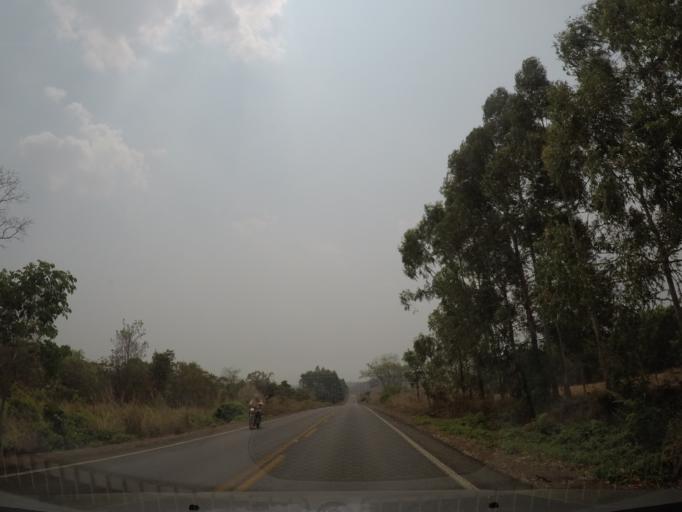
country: BR
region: Goias
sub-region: Pirenopolis
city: Pirenopolis
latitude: -15.9090
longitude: -48.8619
